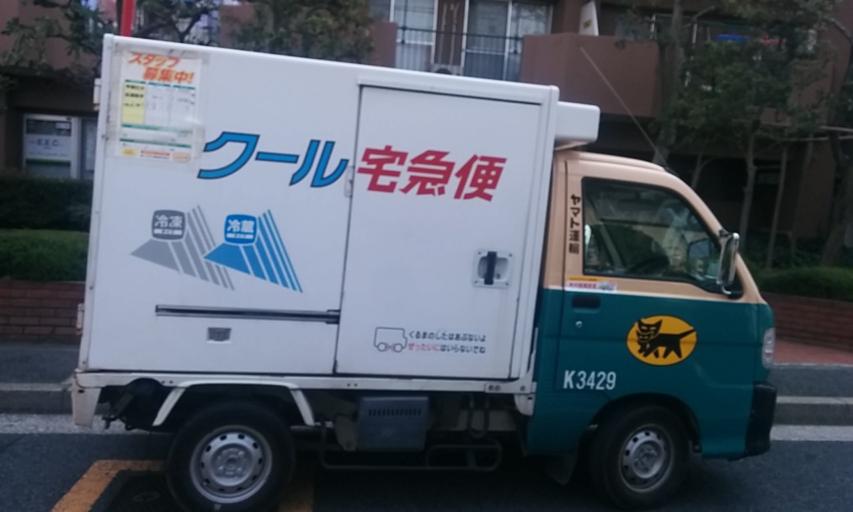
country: JP
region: Tokyo
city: Urayasu
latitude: 35.7035
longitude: 139.8443
